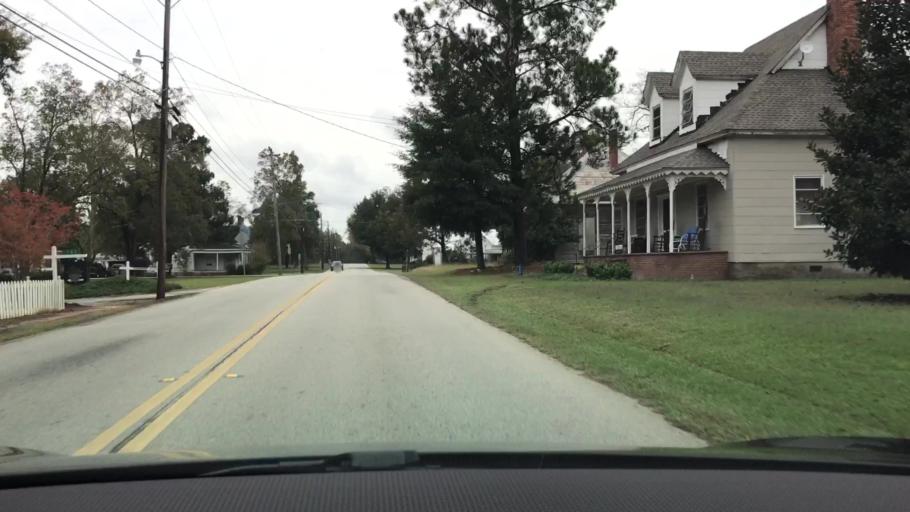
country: US
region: Georgia
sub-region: Jefferson County
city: Wrens
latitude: 33.2120
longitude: -82.4686
